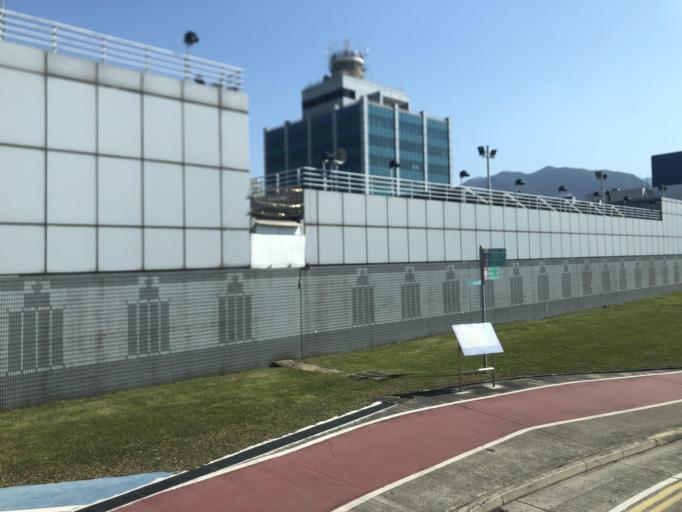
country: HK
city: Tai O
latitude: 22.3027
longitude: 113.9310
